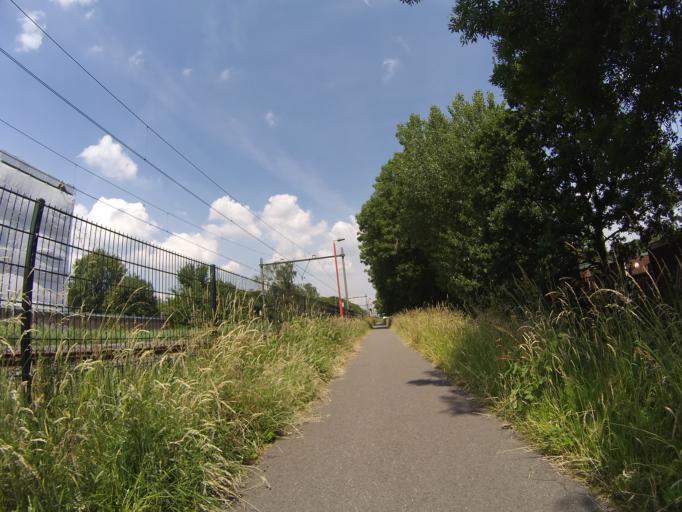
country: NL
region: Utrecht
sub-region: Gemeente Utrecht
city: Utrecht
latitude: 52.1046
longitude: 5.1408
